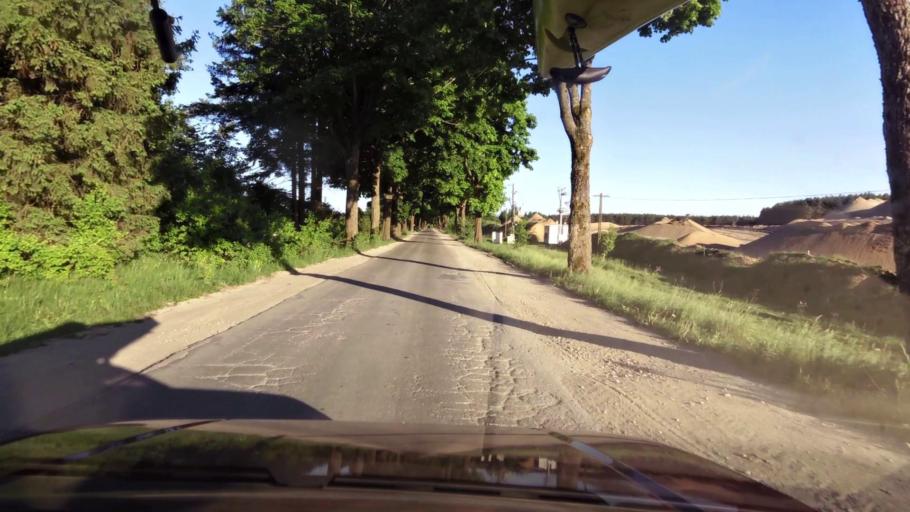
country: PL
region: West Pomeranian Voivodeship
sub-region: Powiat szczecinecki
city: Bialy Bor
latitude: 53.9378
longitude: 16.7916
